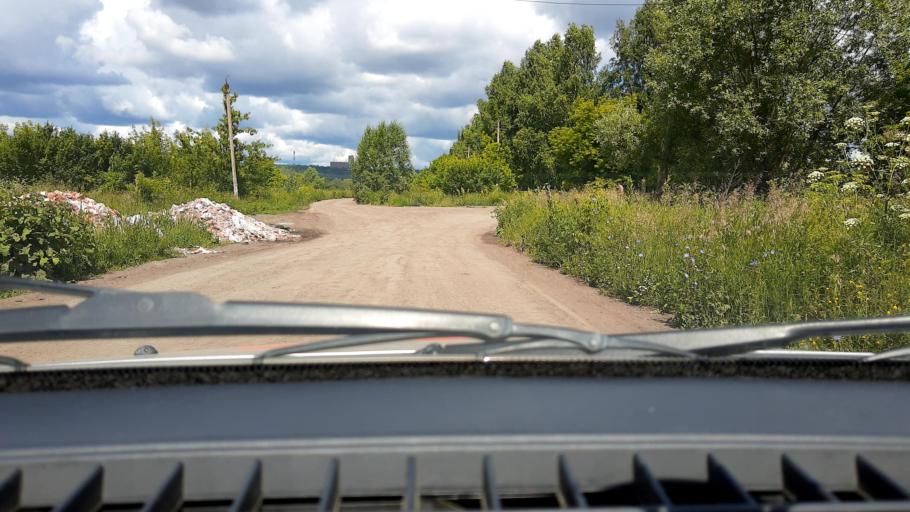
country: RU
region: Bashkortostan
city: Ufa
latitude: 54.6924
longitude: 56.0505
